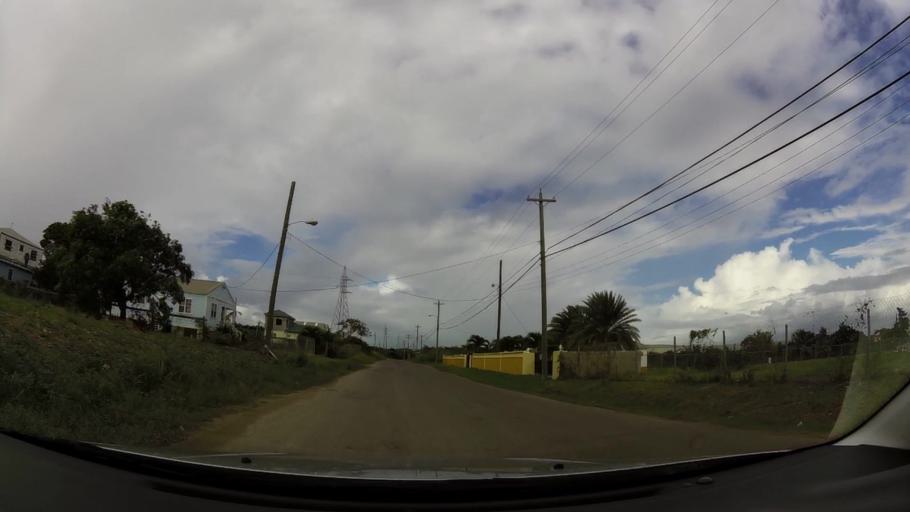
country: AG
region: Saint John
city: Potters Village
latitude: 17.0975
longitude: -61.8130
